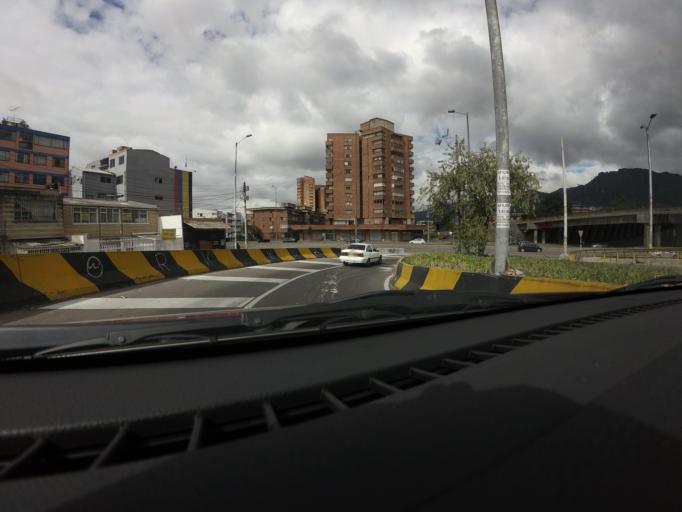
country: CO
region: Bogota D.C.
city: Bogota
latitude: 4.6274
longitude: -74.0813
